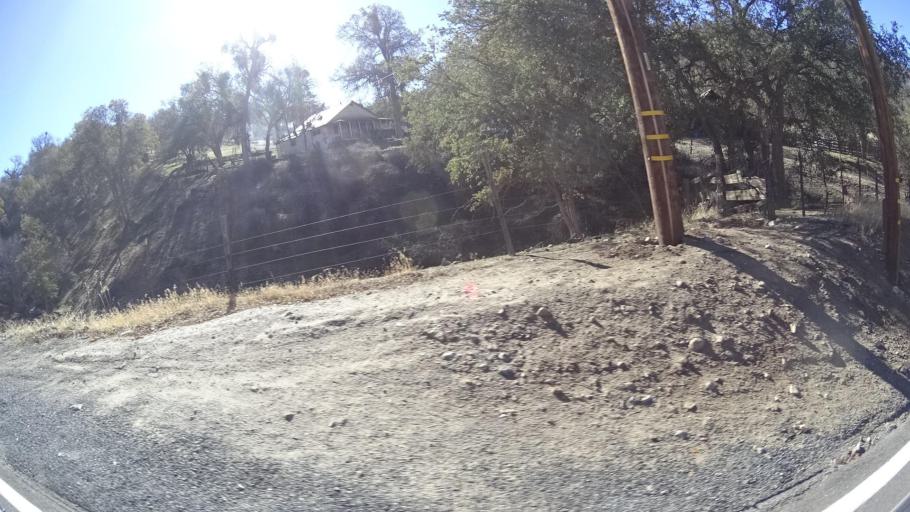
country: US
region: California
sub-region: Kern County
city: Alta Sierra
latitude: 35.7211
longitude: -118.6913
